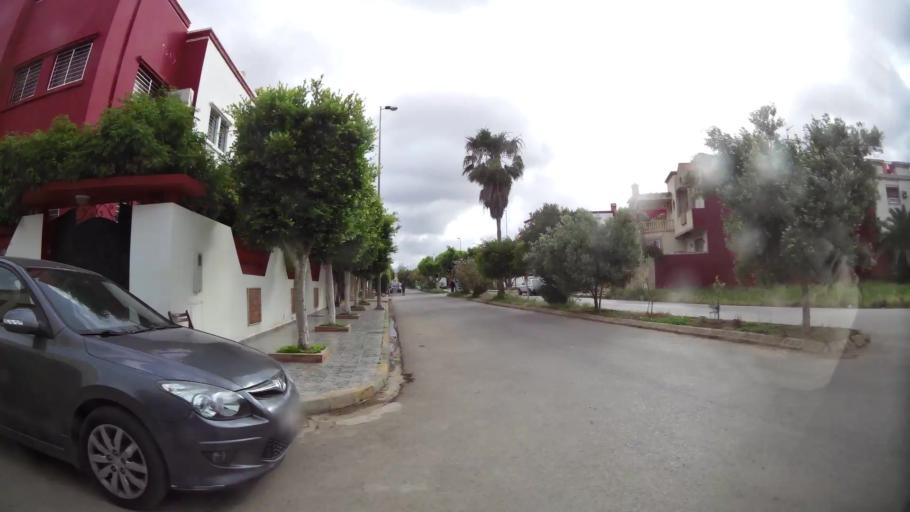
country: MA
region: Oriental
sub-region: Nador
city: Nador
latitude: 35.1646
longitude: -2.9149
